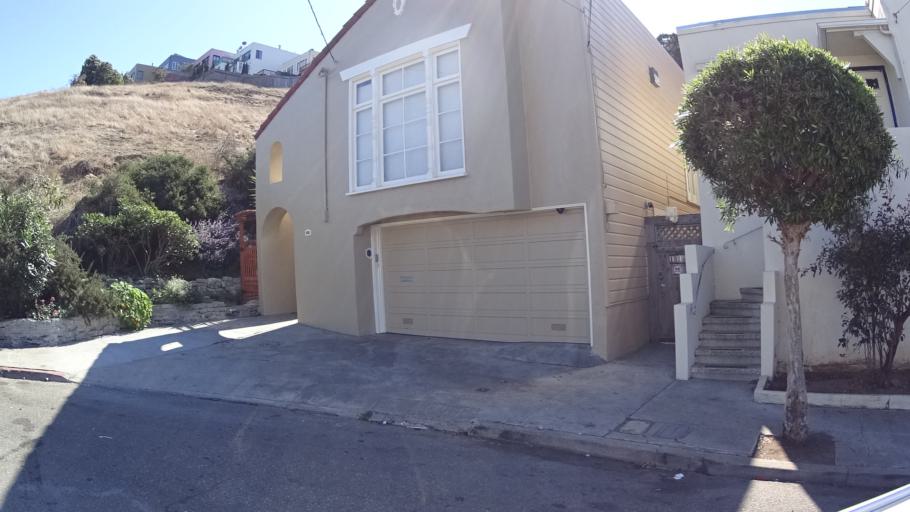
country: US
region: California
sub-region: San Francisco County
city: San Francisco
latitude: 37.7358
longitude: -122.3957
